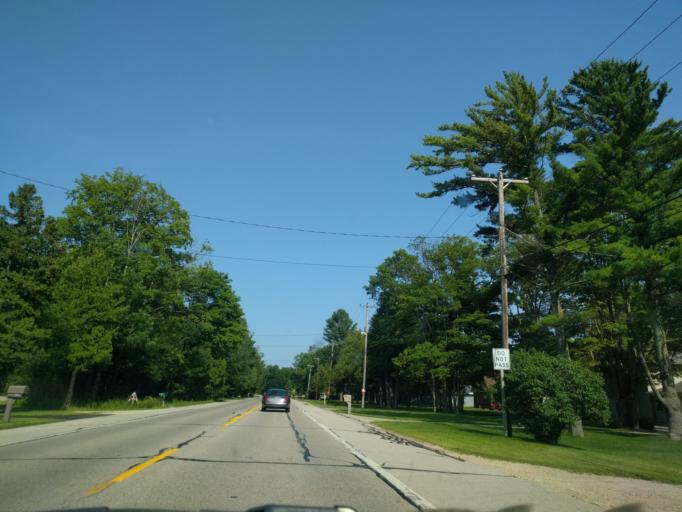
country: US
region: Michigan
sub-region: Delta County
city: Escanaba
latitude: 45.6867
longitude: -87.1083
